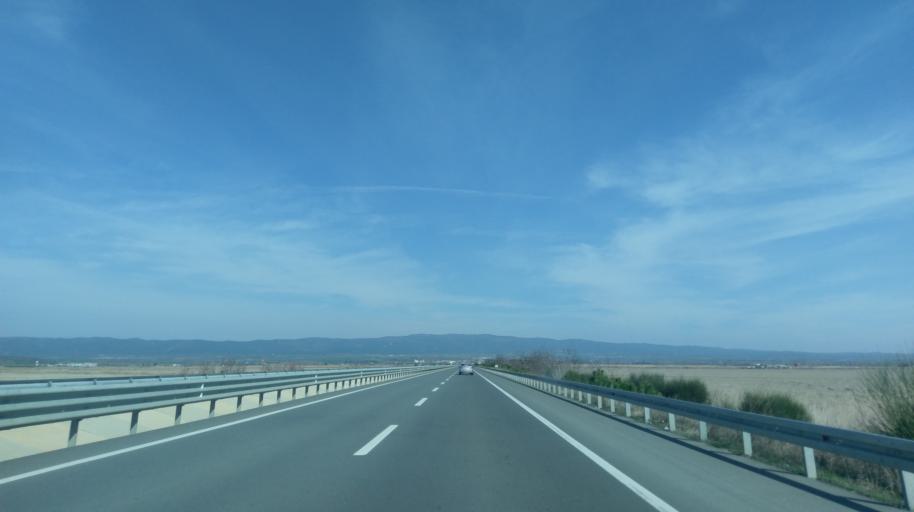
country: TR
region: Canakkale
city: Evrese
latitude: 40.6221
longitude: 26.8677
